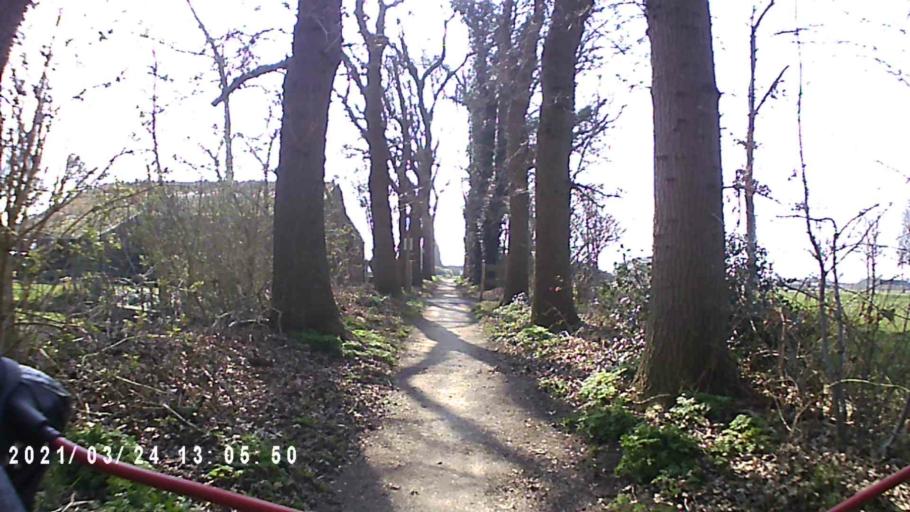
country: NL
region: Groningen
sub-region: Gemeente Leek
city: Leek
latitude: 53.1307
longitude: 6.3068
